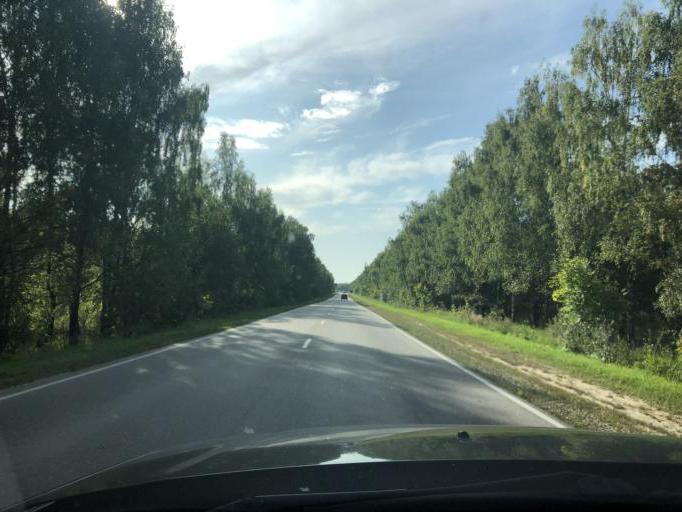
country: RU
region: Tula
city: Leninskiy
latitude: 54.1314
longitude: 37.3124
